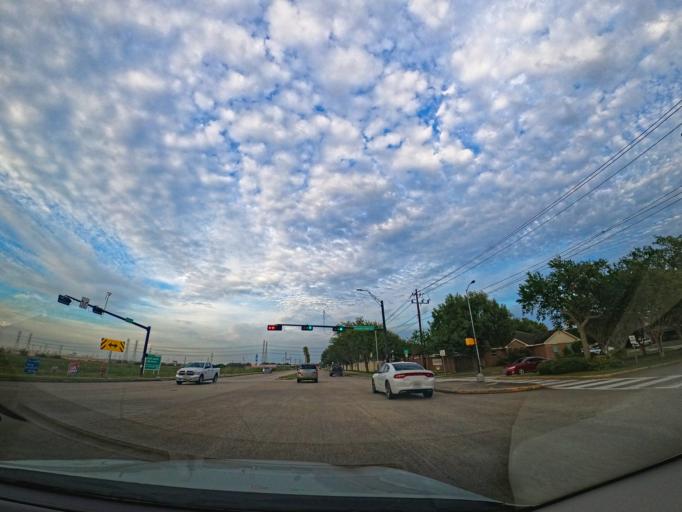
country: US
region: Texas
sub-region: Galveston County
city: Kemah
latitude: 29.5330
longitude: -95.0249
